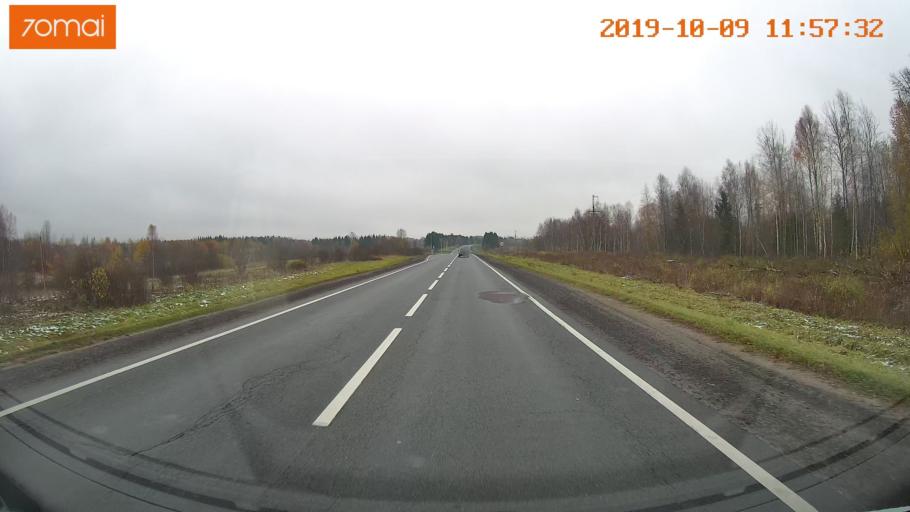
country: RU
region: Vologda
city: Gryazovets
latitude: 58.7310
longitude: 40.2931
